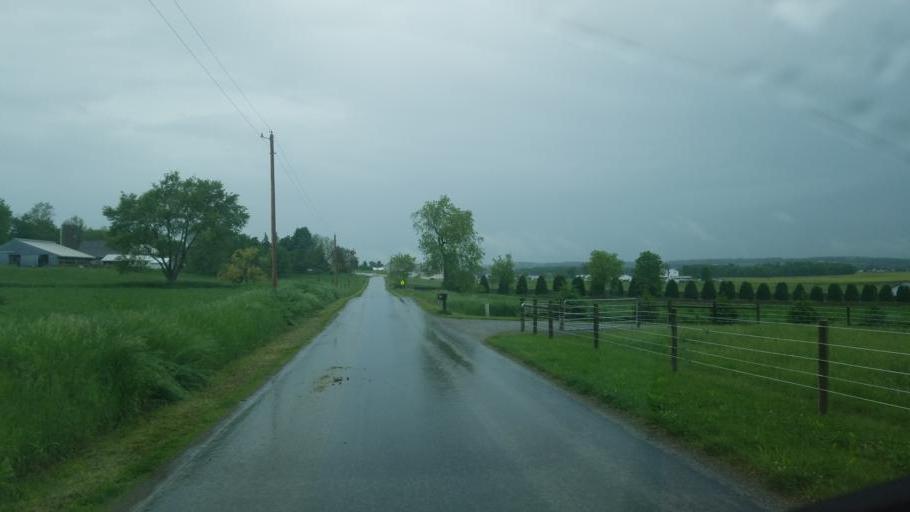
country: US
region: Ohio
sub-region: Wayne County
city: Apple Creek
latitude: 40.7321
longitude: -81.8634
